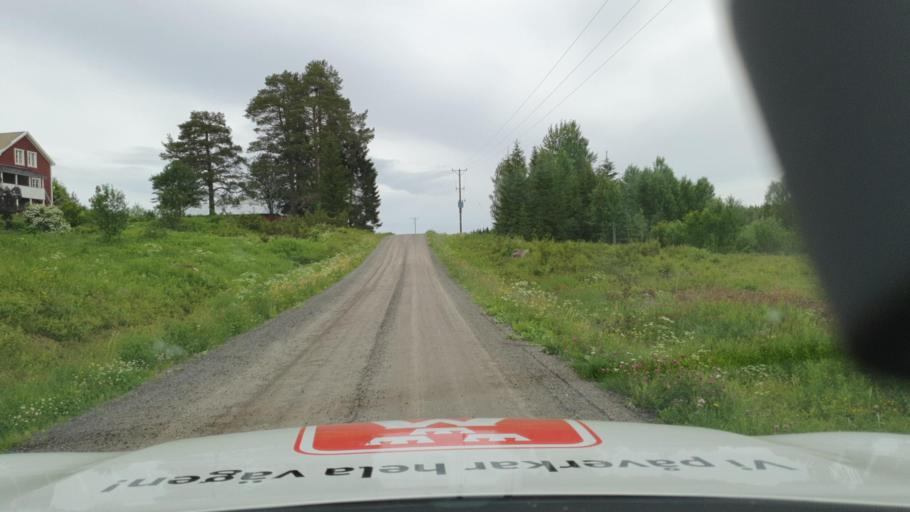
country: SE
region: Vaesterbotten
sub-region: Skelleftea Kommun
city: Burtraesk
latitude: 64.3484
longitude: 20.6093
